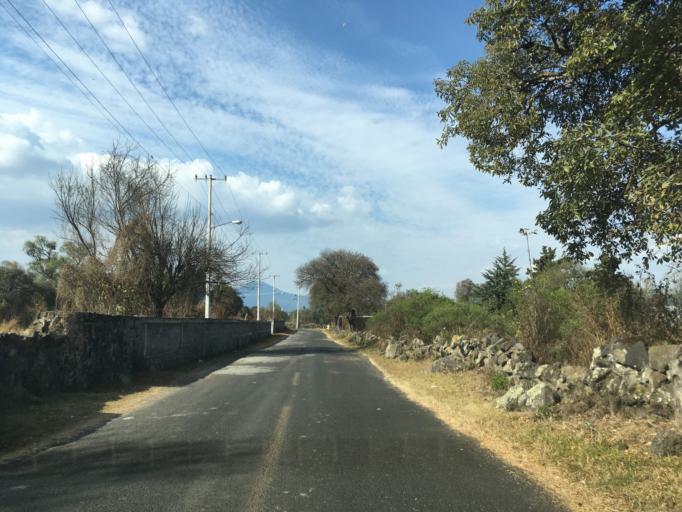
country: MX
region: Michoacan
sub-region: Patzcuaro
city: Santa Ana Chapitiro
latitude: 19.5395
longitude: -101.6392
